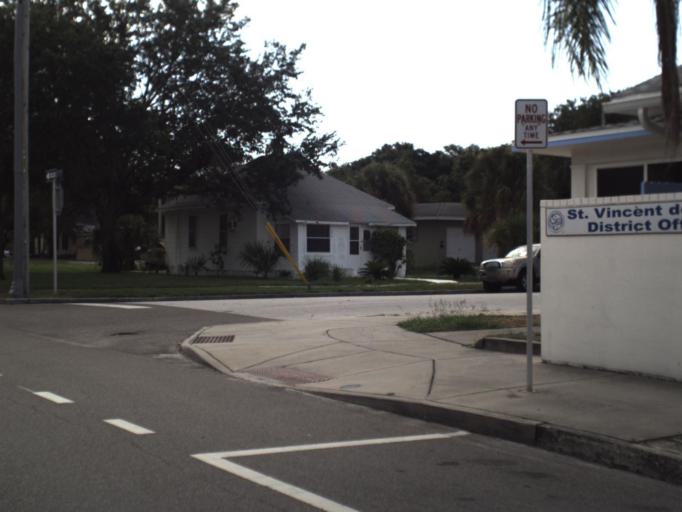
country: US
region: Florida
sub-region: Pinellas County
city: Saint Petersburg
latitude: 27.7764
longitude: -82.6540
